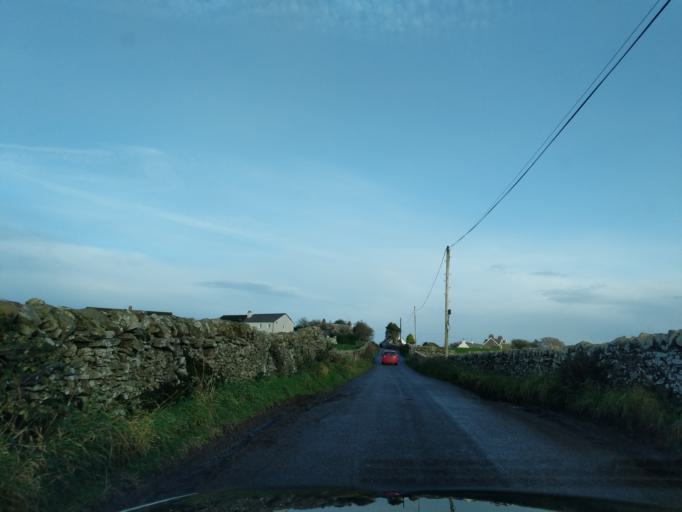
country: GB
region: Scotland
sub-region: Dumfries and Galloway
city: Kirkcudbright
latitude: 54.8127
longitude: -4.1495
